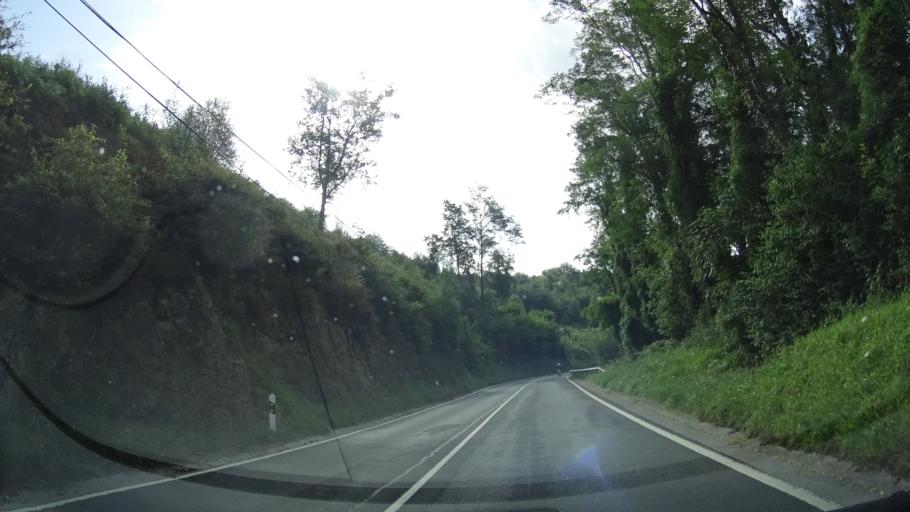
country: ES
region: Basque Country
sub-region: Bizkaia
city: Manaria
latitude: 43.1147
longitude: -2.6474
